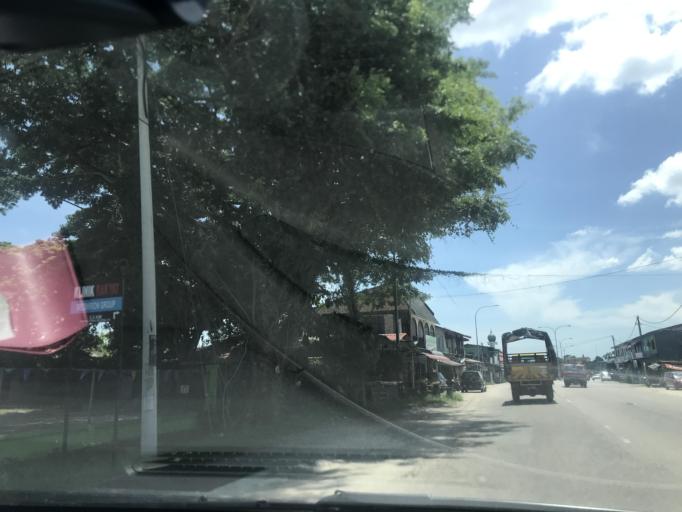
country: MY
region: Kelantan
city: Kota Bharu
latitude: 6.1223
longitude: 102.2714
